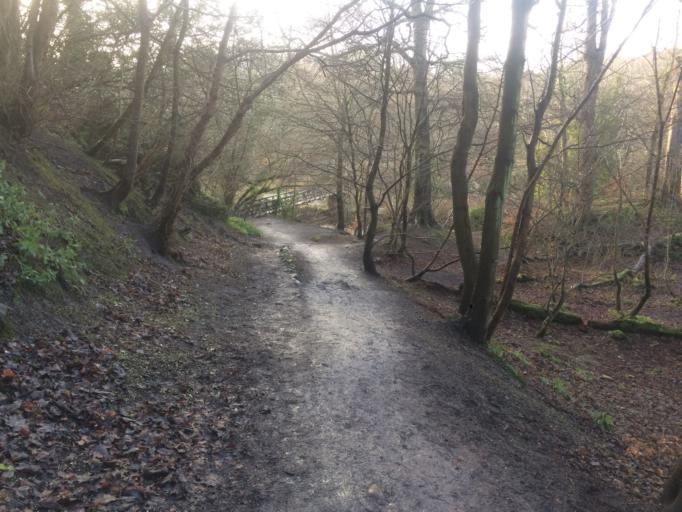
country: GB
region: Scotland
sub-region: Midlothian
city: Loanhead
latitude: 55.8532
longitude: -3.1605
